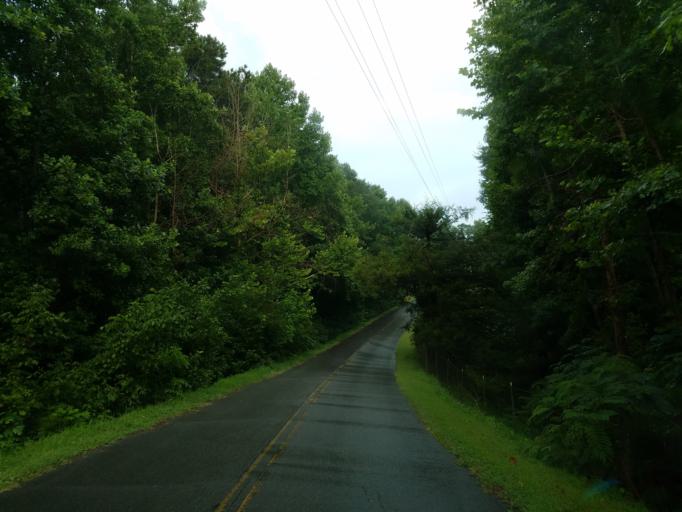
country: US
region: Georgia
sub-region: Bartow County
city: Rydal
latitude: 34.3888
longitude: -84.6551
